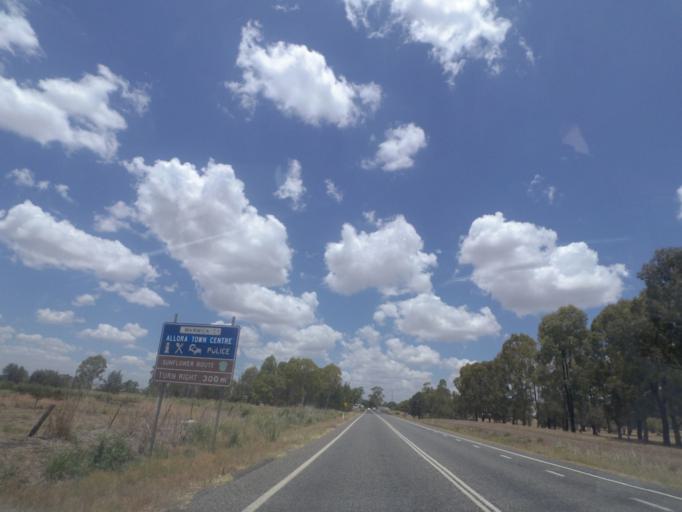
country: AU
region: Queensland
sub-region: Southern Downs
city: Warwick
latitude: -28.0333
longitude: 151.9876
